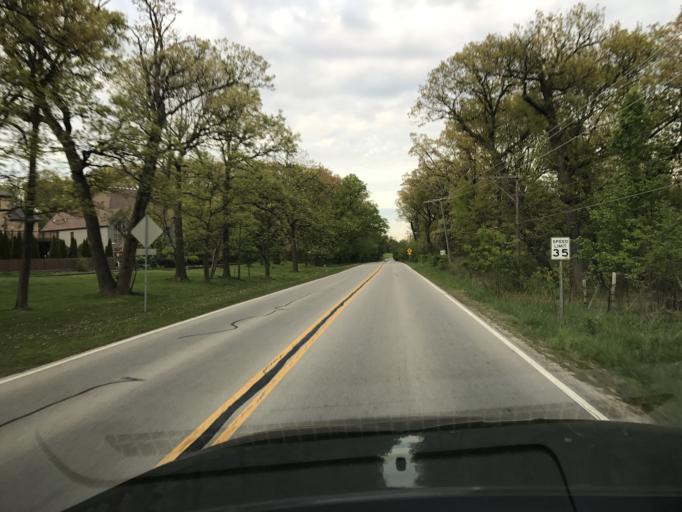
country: US
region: Illinois
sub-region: Will County
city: Bolingbrook
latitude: 41.7183
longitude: -88.1016
